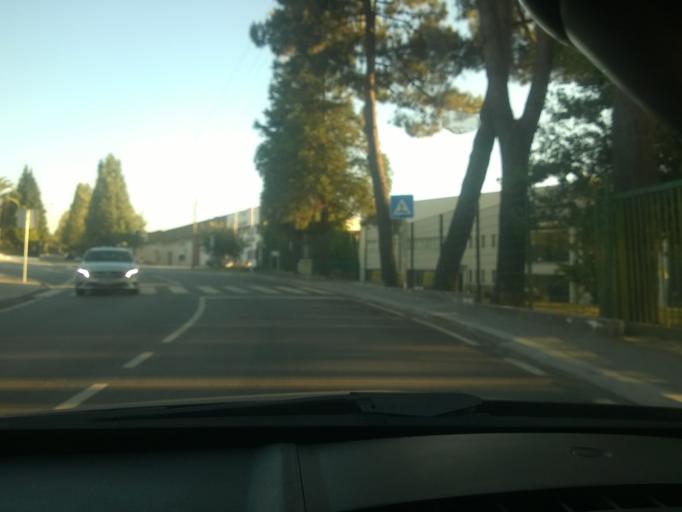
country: PT
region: Porto
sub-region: Maia
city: Gemunde
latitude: 41.2605
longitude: -8.6470
